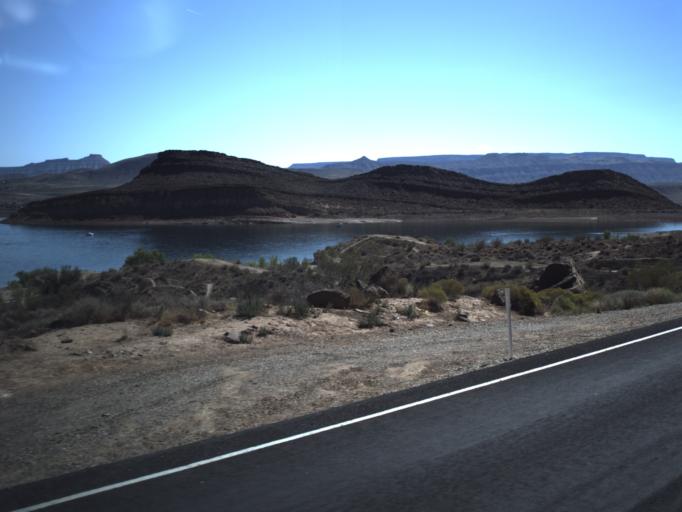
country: US
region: Utah
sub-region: Washington County
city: Hurricane
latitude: 37.1826
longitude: -113.3974
